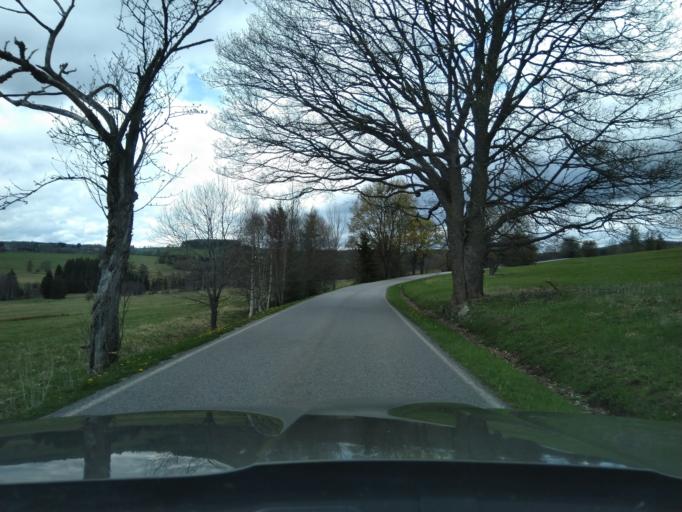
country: CZ
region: Jihocesky
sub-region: Okres Prachatice
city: Borova Lada
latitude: 49.0340
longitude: 13.6662
